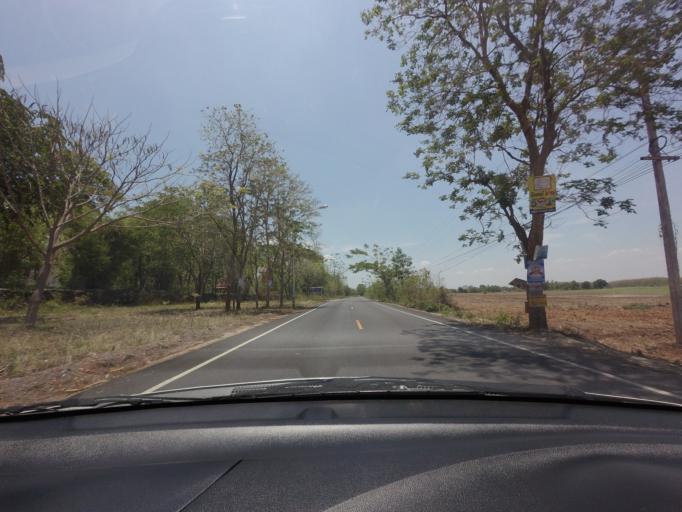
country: TH
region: Suphan Buri
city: Dan Chang
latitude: 14.8756
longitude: 99.7031
